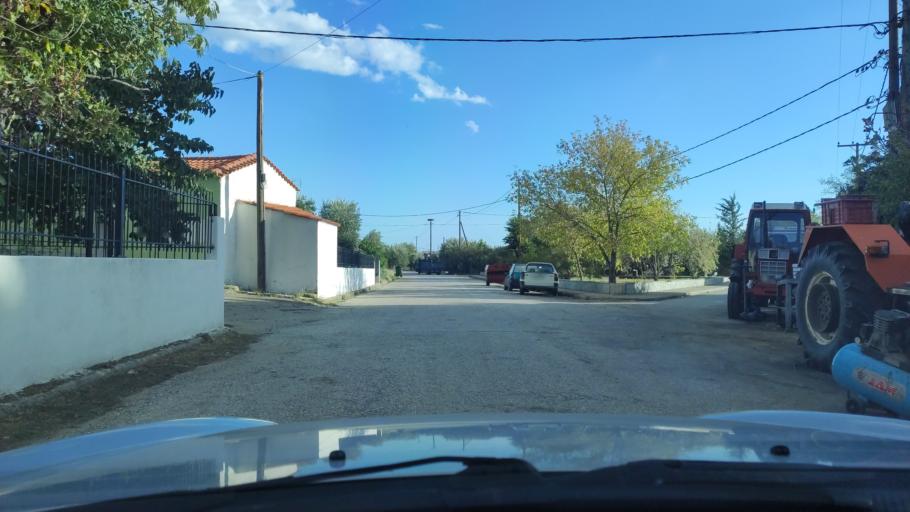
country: GR
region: East Macedonia and Thrace
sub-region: Nomos Xanthis
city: Selero
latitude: 41.1250
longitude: 25.0643
